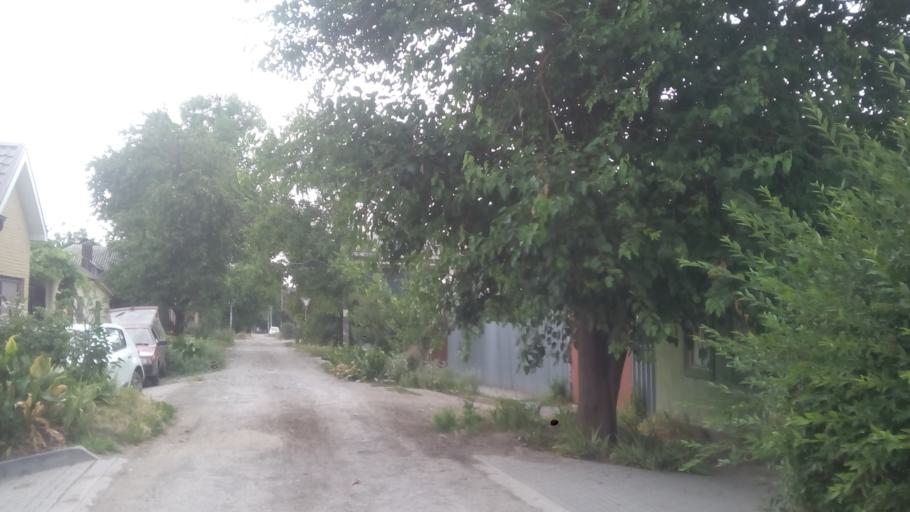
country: RU
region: Rostov
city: Rostov-na-Donu
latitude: 47.2187
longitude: 39.6412
